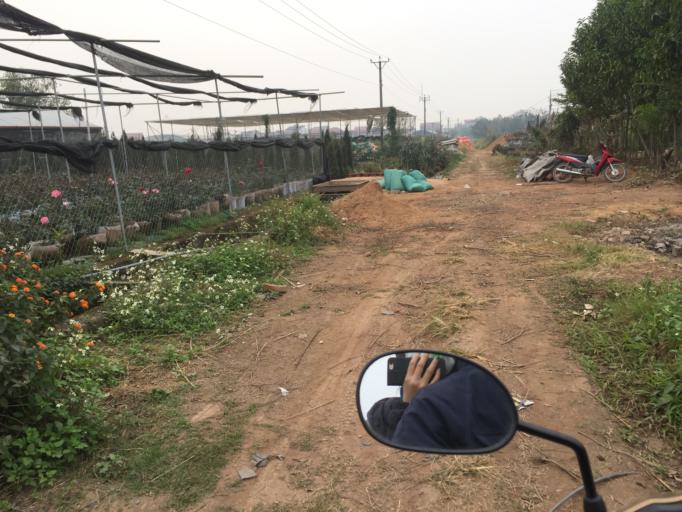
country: VN
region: Hung Yen
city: Van Giang
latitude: 20.9656
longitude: 105.9100
